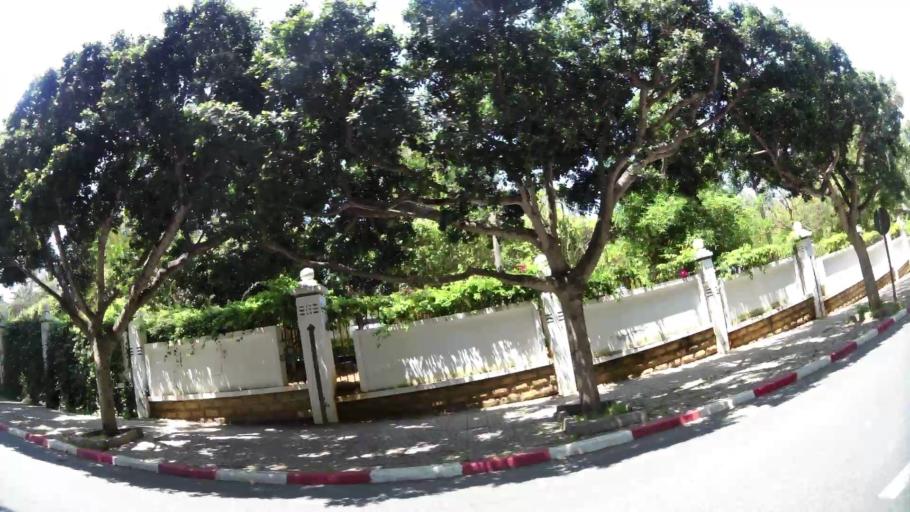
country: MA
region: Rabat-Sale-Zemmour-Zaer
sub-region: Rabat
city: Rabat
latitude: 34.0111
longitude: -6.8257
